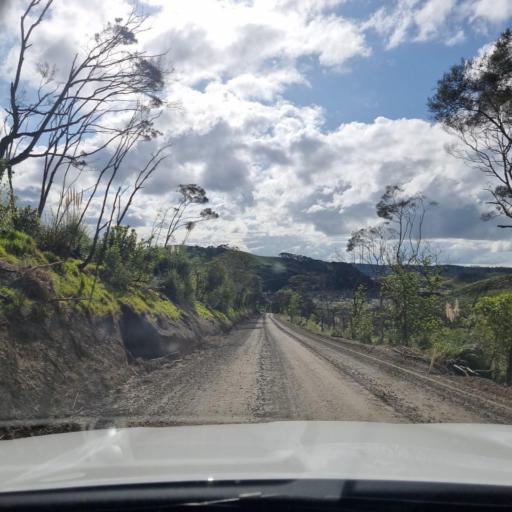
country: NZ
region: Auckland
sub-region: Auckland
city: Wellsford
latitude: -36.3089
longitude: 174.1233
